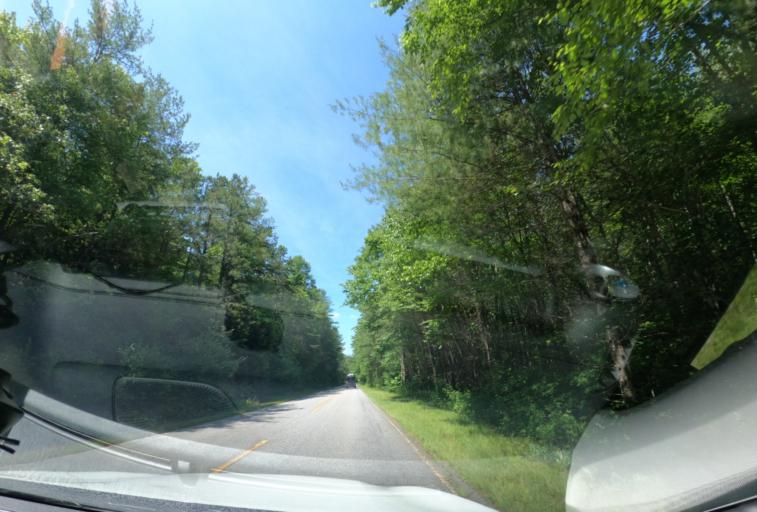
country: US
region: North Carolina
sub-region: Transylvania County
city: Brevard
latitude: 35.1630
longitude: -82.6400
